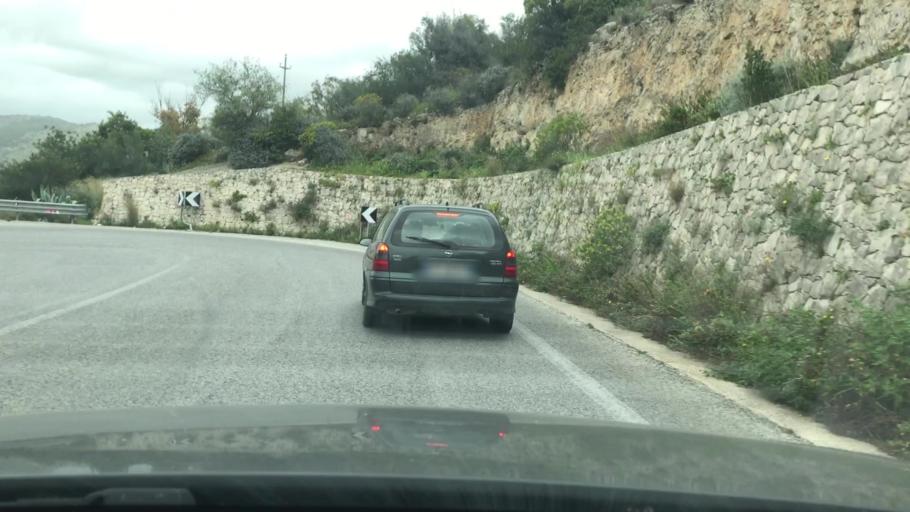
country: IT
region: Sicily
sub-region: Ragusa
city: Scicli
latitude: 36.7977
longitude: 14.7102
